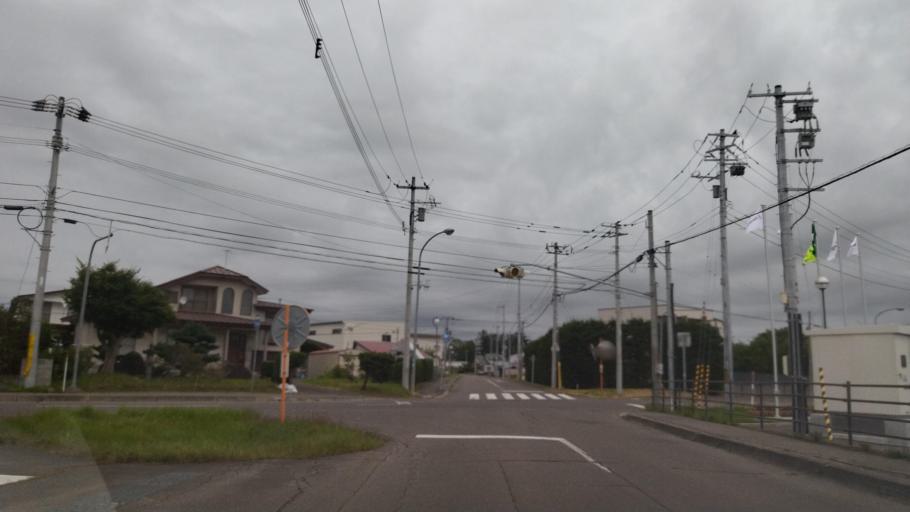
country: JP
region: Hokkaido
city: Otofuke
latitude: 43.2254
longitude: 143.2875
